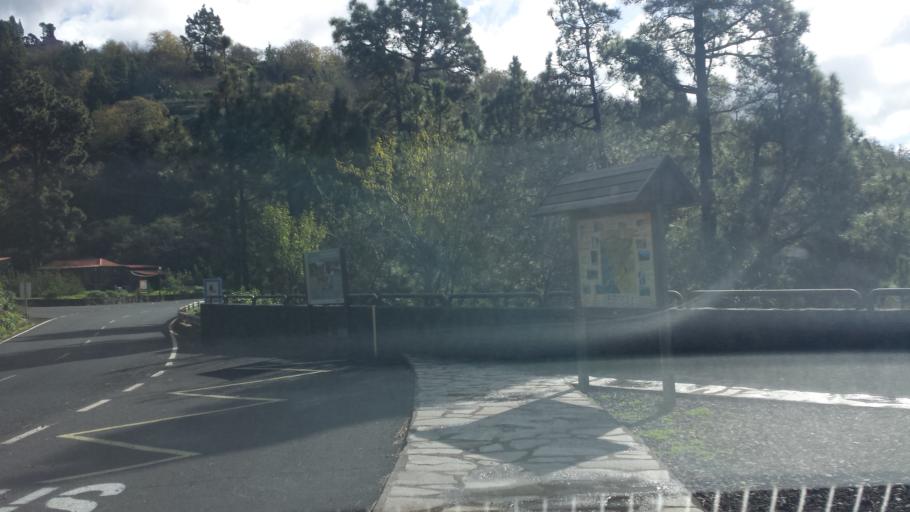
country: ES
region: Canary Islands
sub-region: Provincia de Santa Cruz de Tenerife
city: Puntagorda
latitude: 28.7472
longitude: -17.9676
